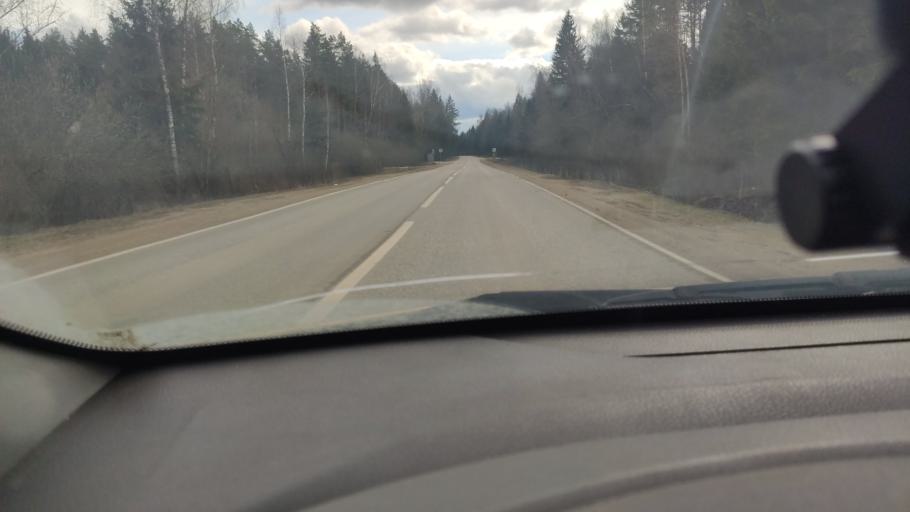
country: RU
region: Moskovskaya
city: Ruza
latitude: 55.7244
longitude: 36.1579
